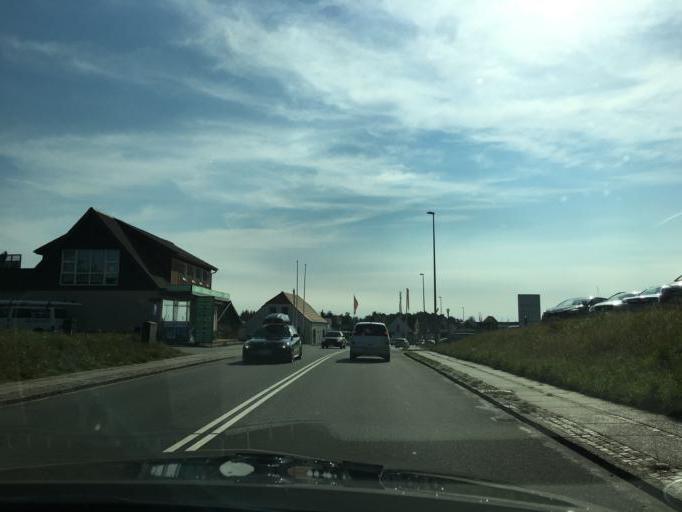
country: DK
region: Central Jutland
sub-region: Ringkobing-Skjern Kommune
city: Hvide Sande
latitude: 55.8171
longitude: 8.1919
